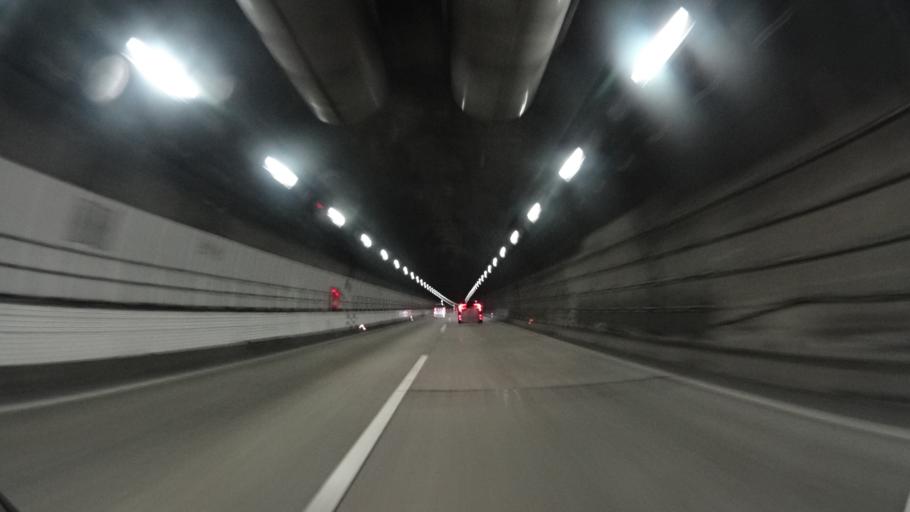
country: JP
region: Hyogo
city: Himeji
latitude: 34.8797
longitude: 134.6440
